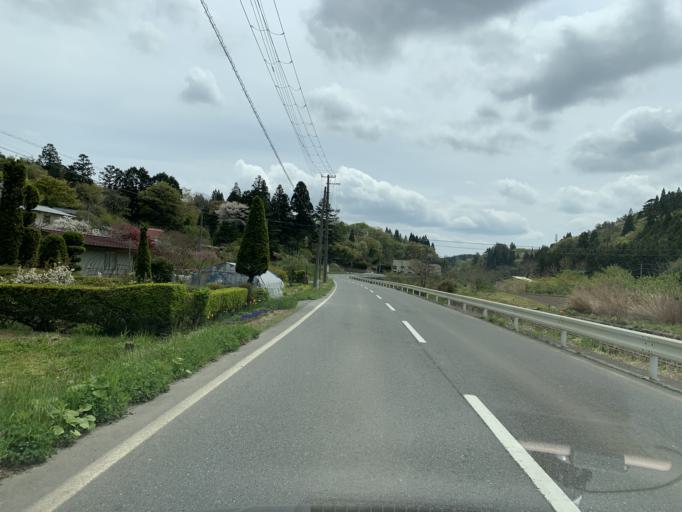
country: JP
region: Iwate
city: Ichinoseki
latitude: 38.8089
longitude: 141.3817
